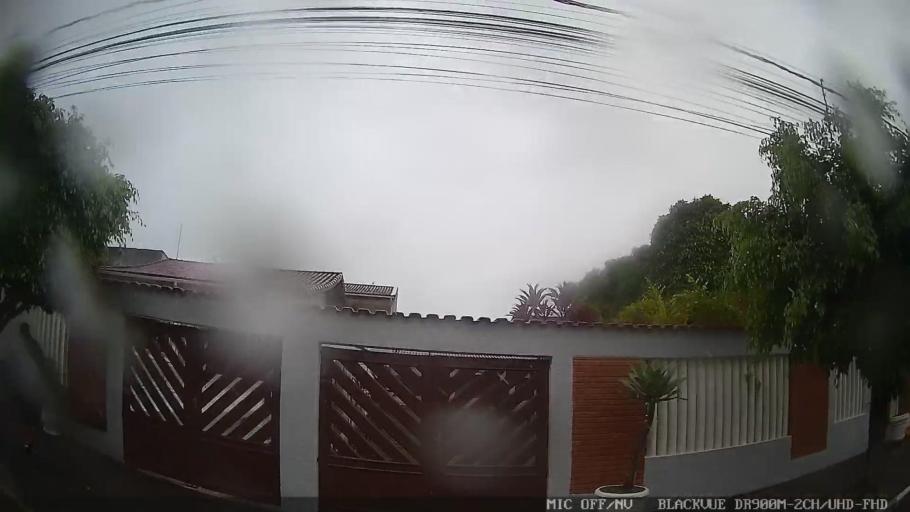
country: BR
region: Sao Paulo
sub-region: Itanhaem
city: Itanhaem
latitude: -24.1886
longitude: -46.8178
